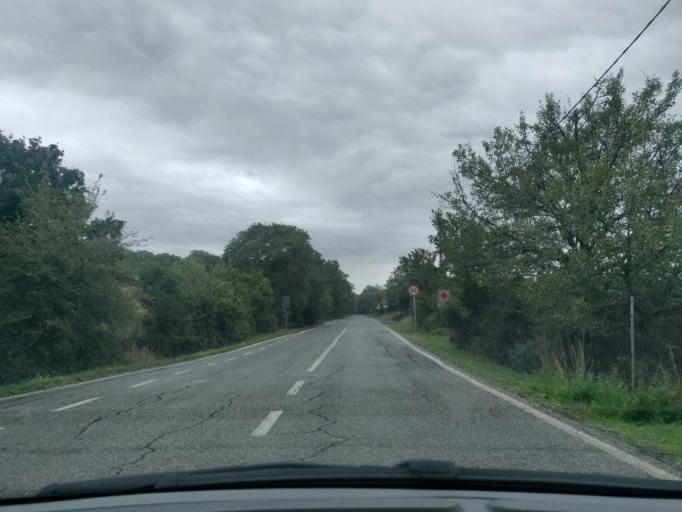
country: IT
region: Latium
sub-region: Citta metropolitana di Roma Capitale
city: Allumiere
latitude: 42.1259
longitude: 11.8646
